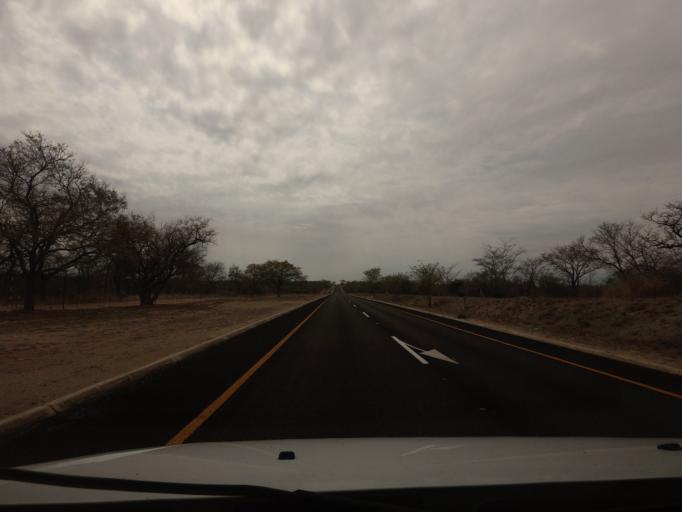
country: ZA
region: Limpopo
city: Thulamahashi
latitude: -24.5564
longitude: 31.2177
